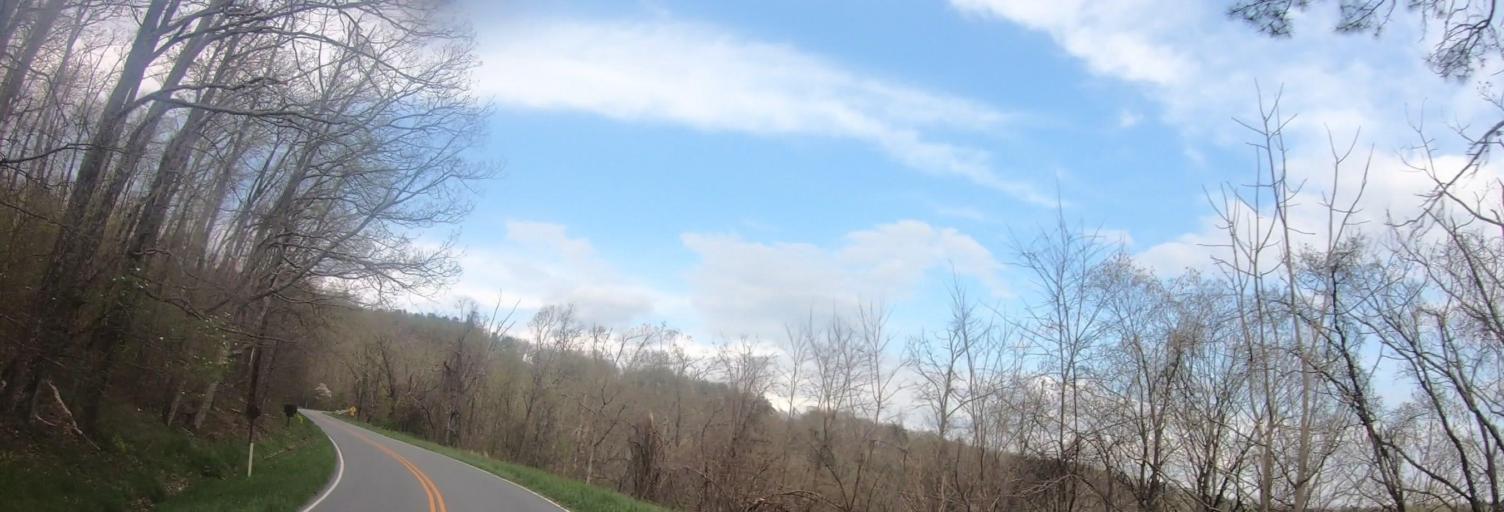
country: US
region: Virginia
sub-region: Rockingham County
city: Grottoes
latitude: 38.2059
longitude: -78.7447
